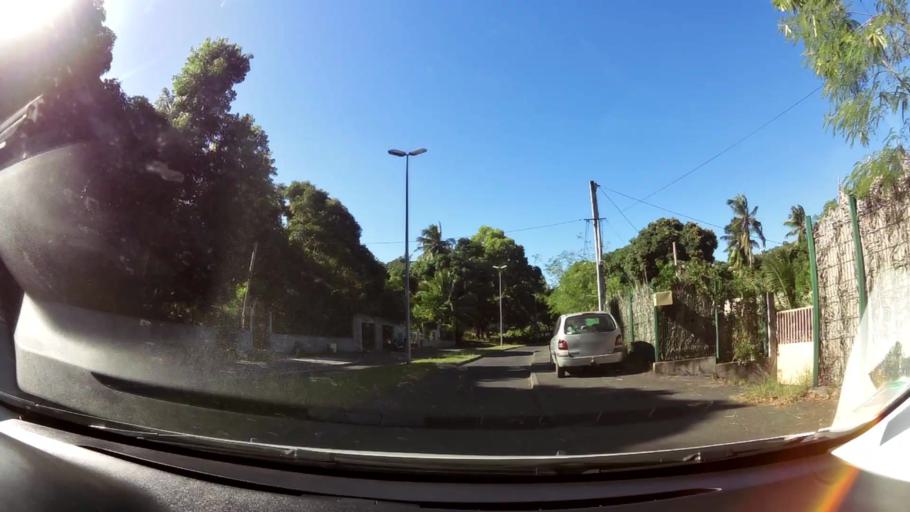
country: YT
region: Pamandzi
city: Pamandzi
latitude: -12.7929
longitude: 45.2777
